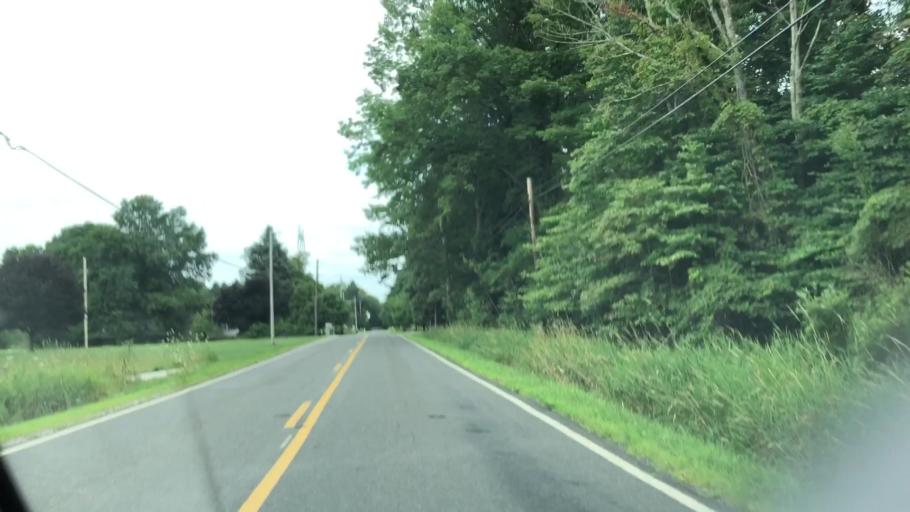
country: US
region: Ohio
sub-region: Summit County
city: Montrose-Ghent
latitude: 41.1177
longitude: -81.7006
